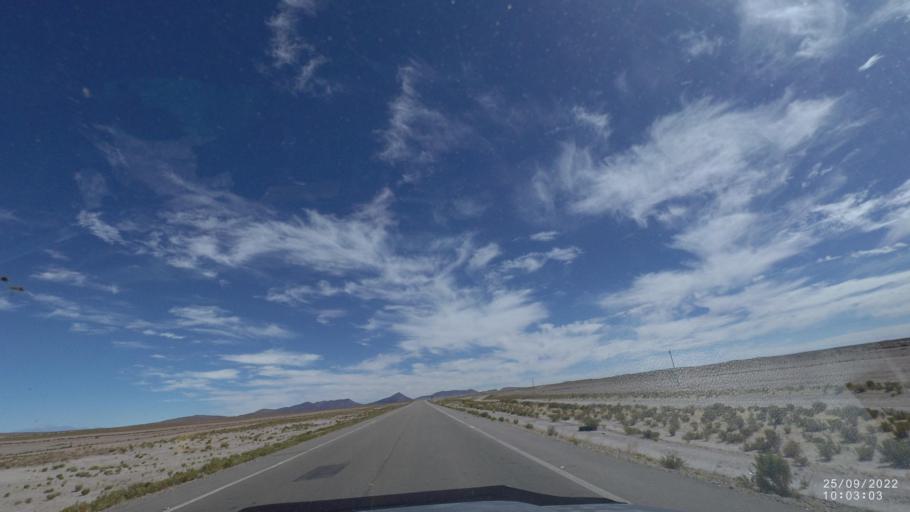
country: BO
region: Potosi
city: Colchani
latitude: -20.2253
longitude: -66.9554
